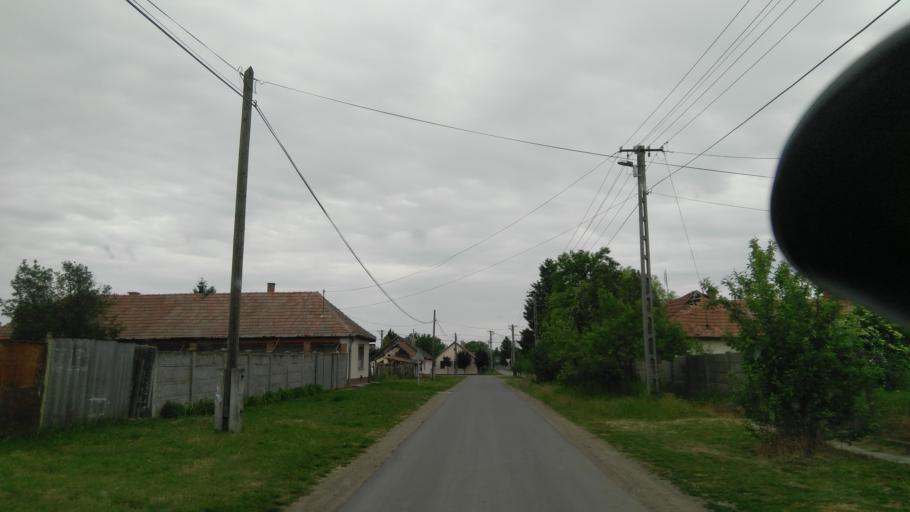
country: HU
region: Bekes
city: Doboz
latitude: 46.7276
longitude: 21.2473
